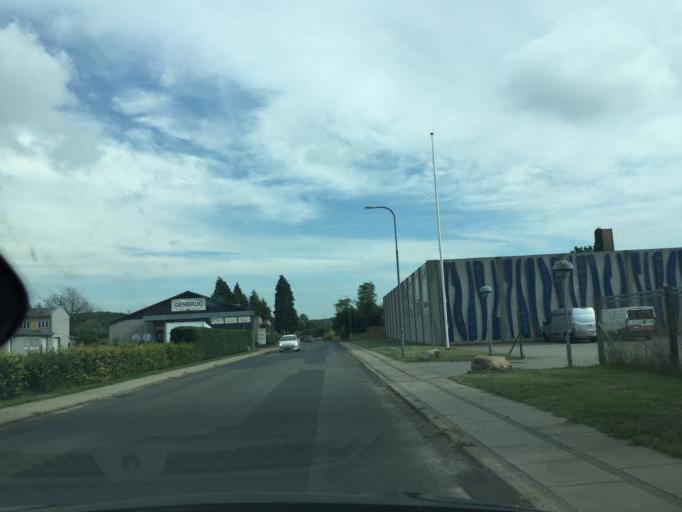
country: DK
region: South Denmark
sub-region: Faaborg-Midtfyn Kommune
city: Arslev
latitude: 55.3038
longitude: 10.4732
